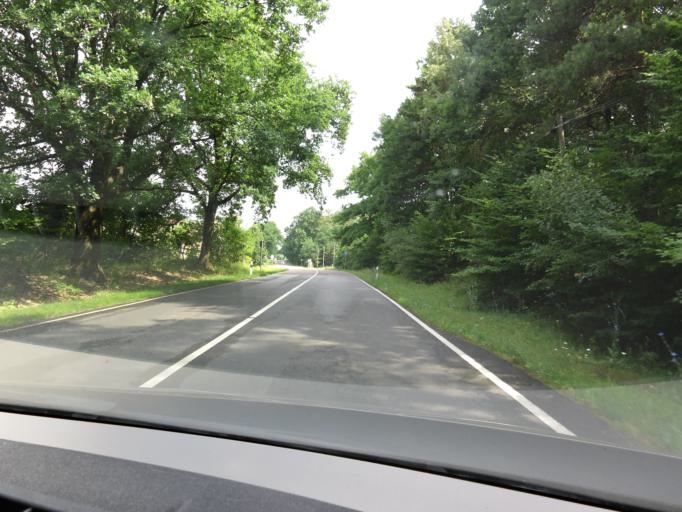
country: DE
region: Saxony-Anhalt
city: Kemberg
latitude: 51.7460
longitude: 12.6296
